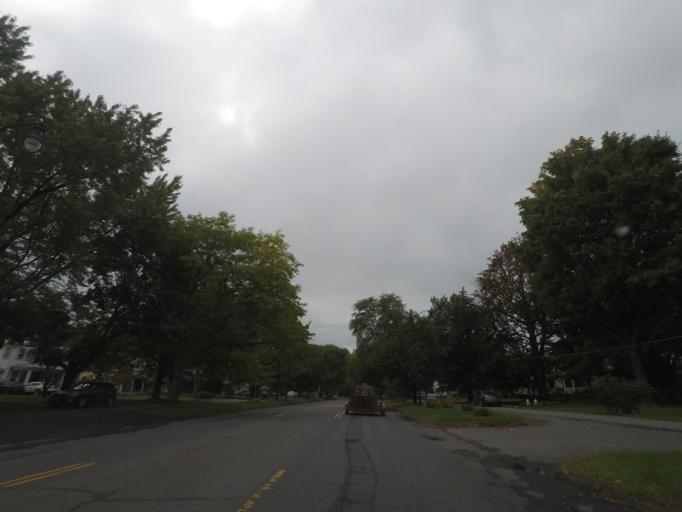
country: US
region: New York
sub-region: Albany County
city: West Albany
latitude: 42.6699
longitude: -73.7938
